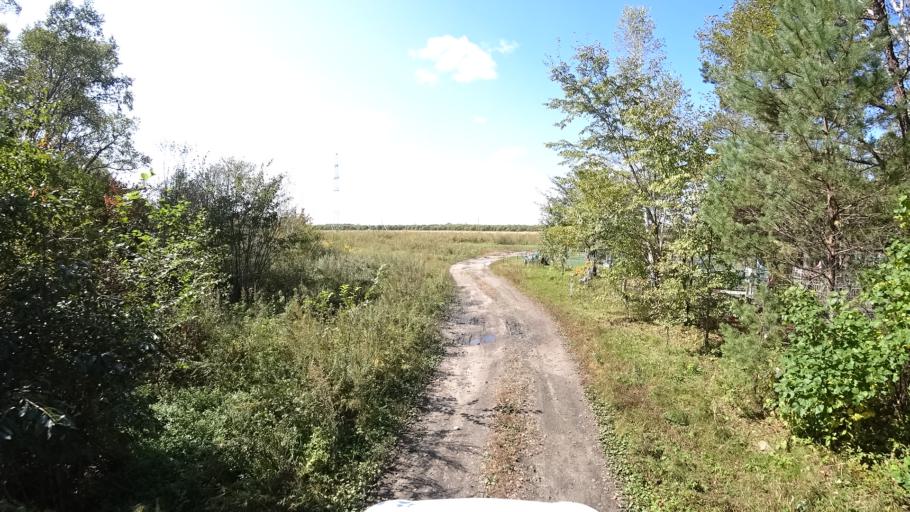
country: RU
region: Amur
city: Arkhara
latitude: 49.4000
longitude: 130.1217
